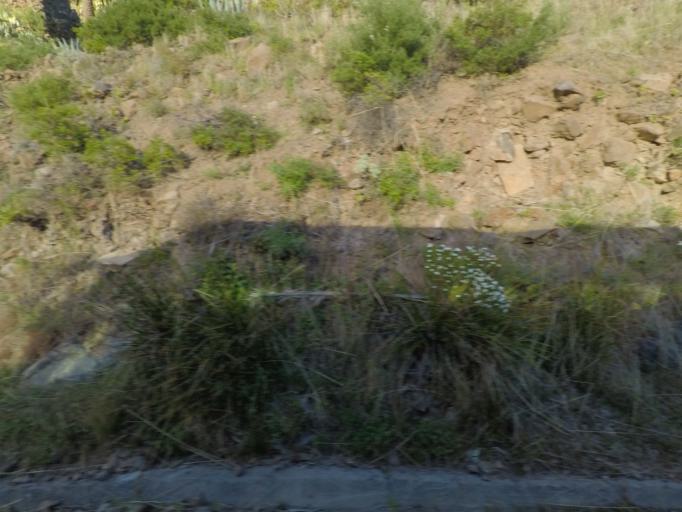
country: ES
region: Canary Islands
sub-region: Provincia de Santa Cruz de Tenerife
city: Alajero
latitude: 28.0949
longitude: -17.1973
